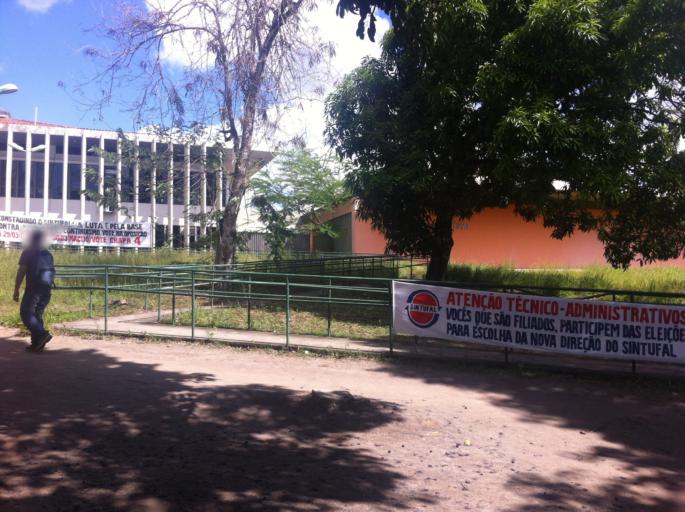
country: BR
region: Alagoas
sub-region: Satuba
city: Satuba
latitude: -9.5552
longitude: -35.7767
